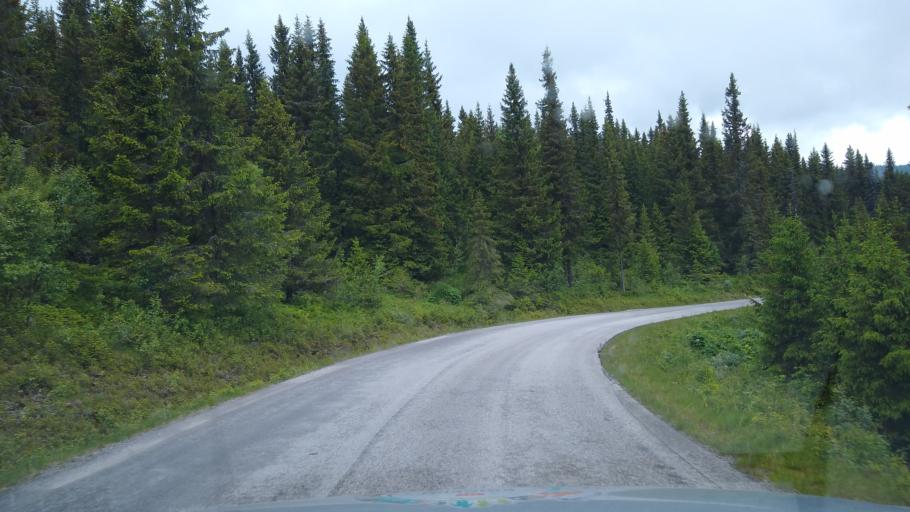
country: NO
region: Oppland
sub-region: Ringebu
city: Ringebu
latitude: 61.4847
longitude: 10.1168
